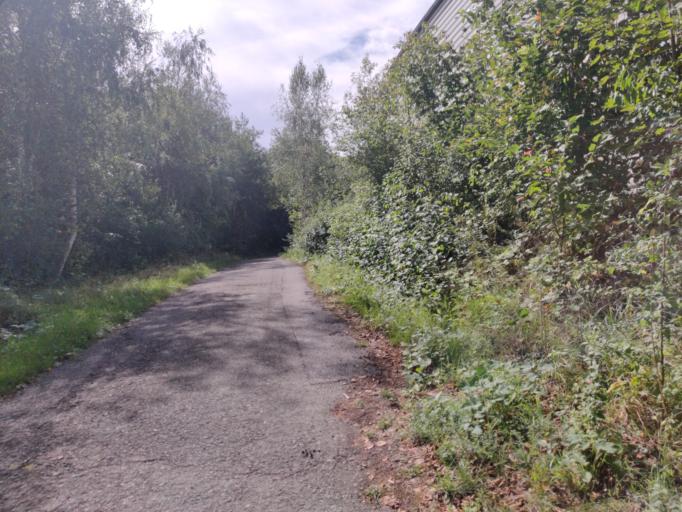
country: DE
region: Lower Saxony
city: Langelsheim
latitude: 51.9661
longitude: 10.3652
